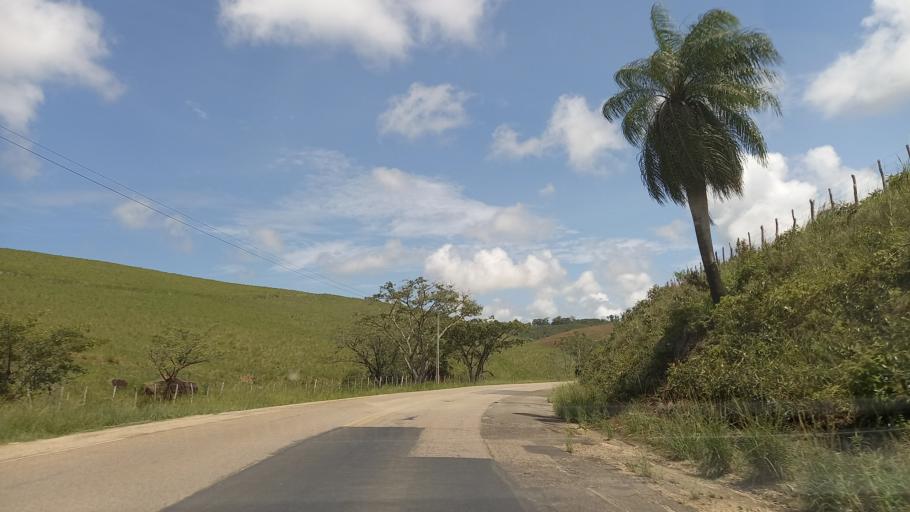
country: BR
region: Pernambuco
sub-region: Barreiros
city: Barreiros
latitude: -8.7556
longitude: -35.1708
